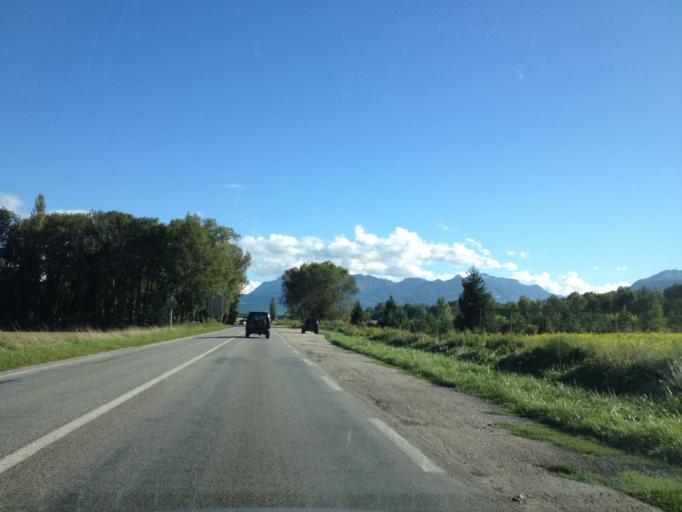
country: FR
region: Rhone-Alpes
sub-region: Departement de la Savoie
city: Le Bourget-du-Lac
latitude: 45.6364
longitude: 5.8719
